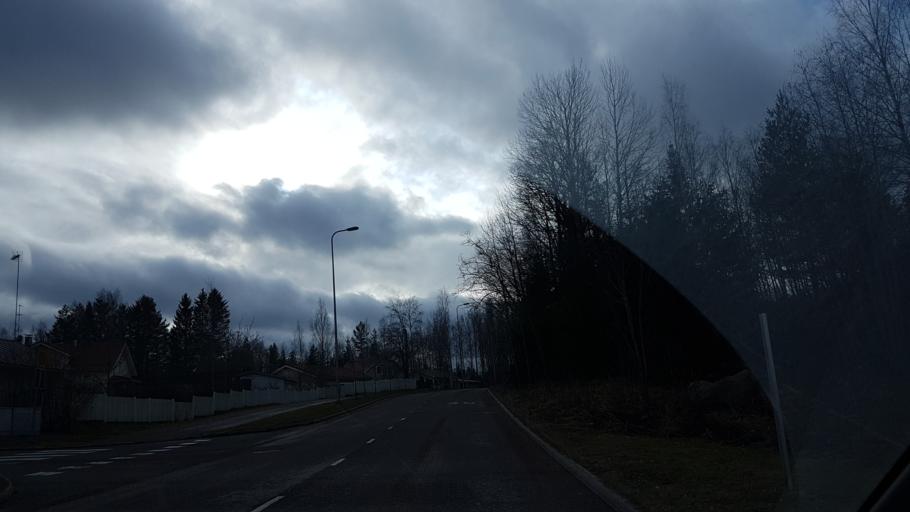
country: FI
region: Uusimaa
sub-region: Helsinki
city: Kauniainen
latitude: 60.3263
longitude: 24.7166
